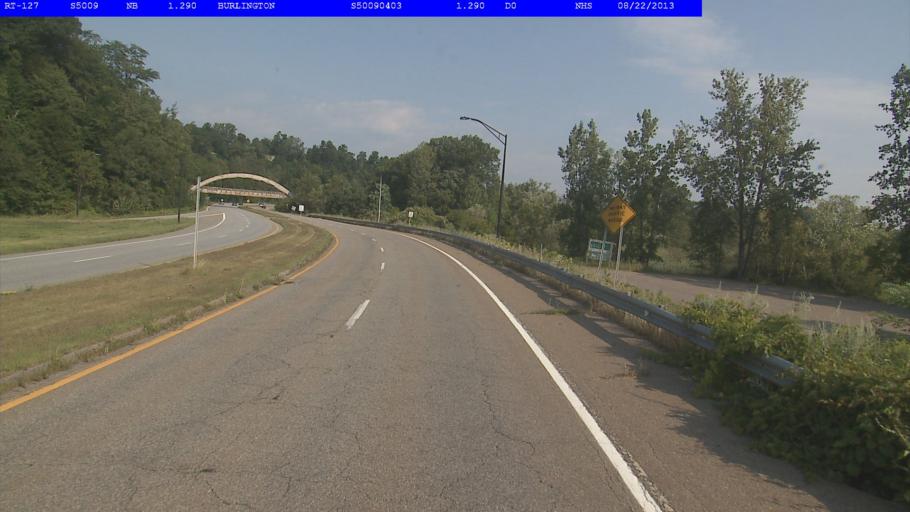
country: US
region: Vermont
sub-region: Chittenden County
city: Burlington
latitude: 44.5038
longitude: -73.2311
